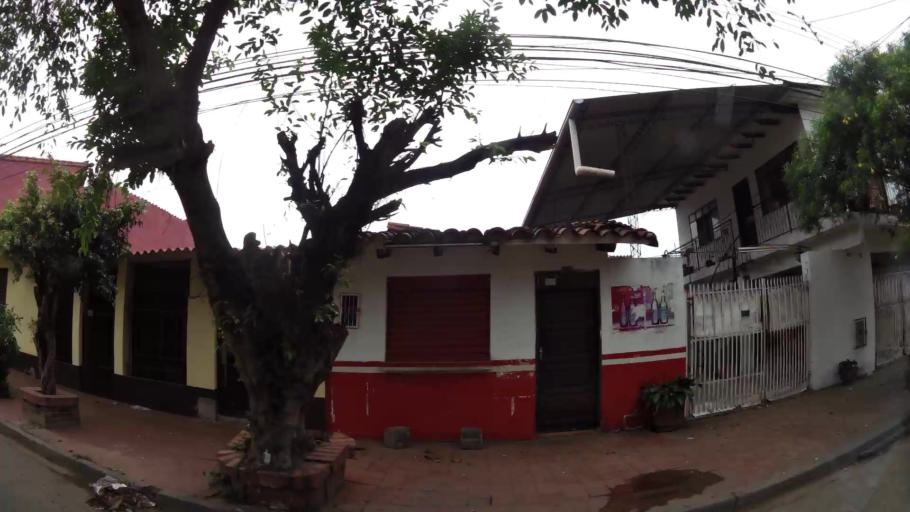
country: BO
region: Santa Cruz
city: Santa Cruz de la Sierra
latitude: -17.7652
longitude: -63.1631
